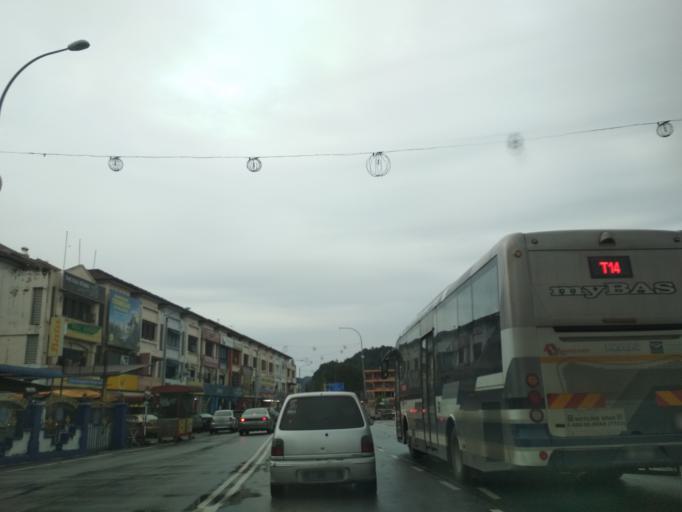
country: MY
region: Perlis
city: Kangar
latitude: 6.4378
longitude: 100.1940
